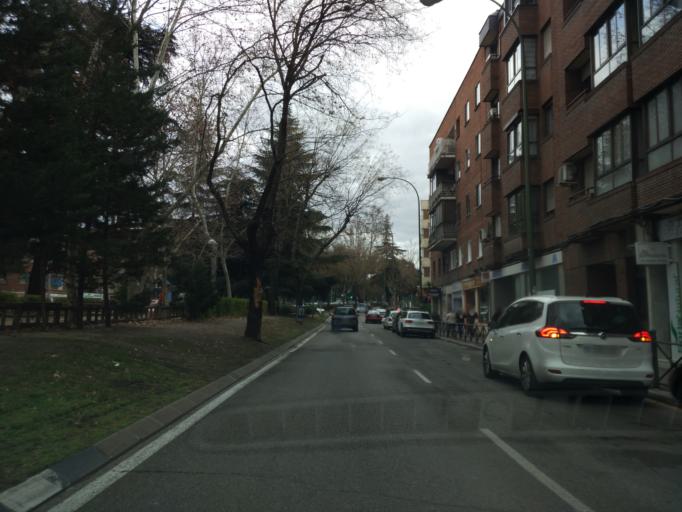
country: ES
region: Madrid
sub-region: Provincia de Madrid
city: Ciudad Lineal
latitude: 40.4588
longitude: -3.6596
